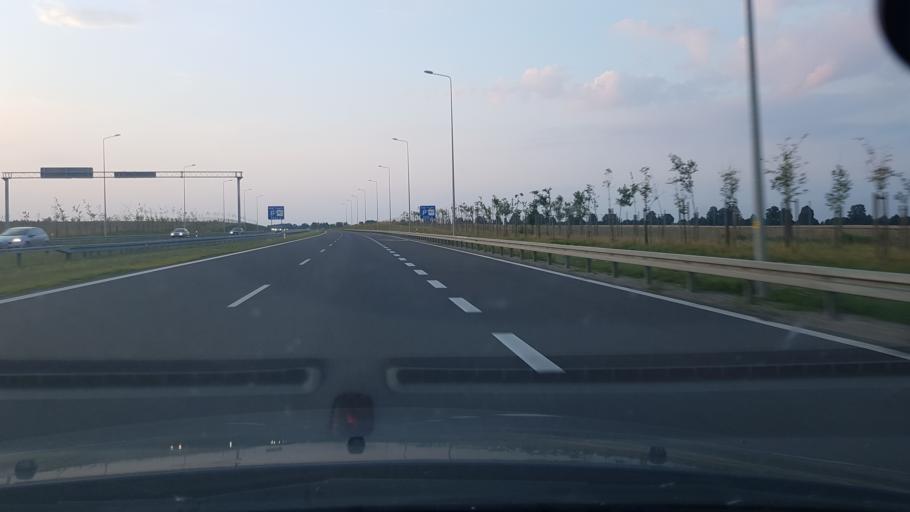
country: PL
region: Warmian-Masurian Voivodeship
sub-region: Powiat nidzicki
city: Nidzica
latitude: 53.2793
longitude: 20.4380
